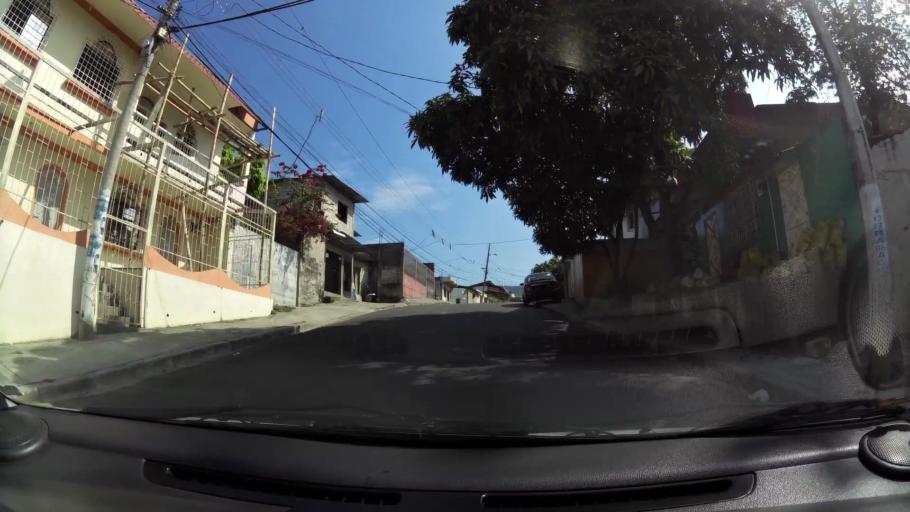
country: EC
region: Guayas
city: Guayaquil
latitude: -2.1536
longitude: -79.9369
